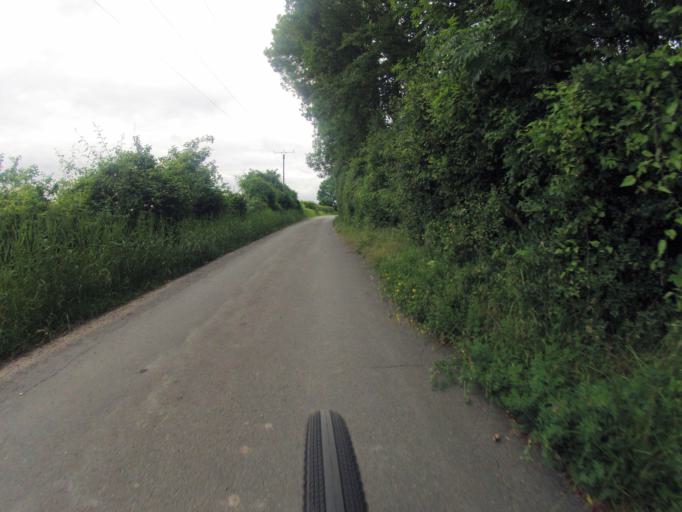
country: DE
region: North Rhine-Westphalia
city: Ibbenburen
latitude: 52.2369
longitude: 7.7019
